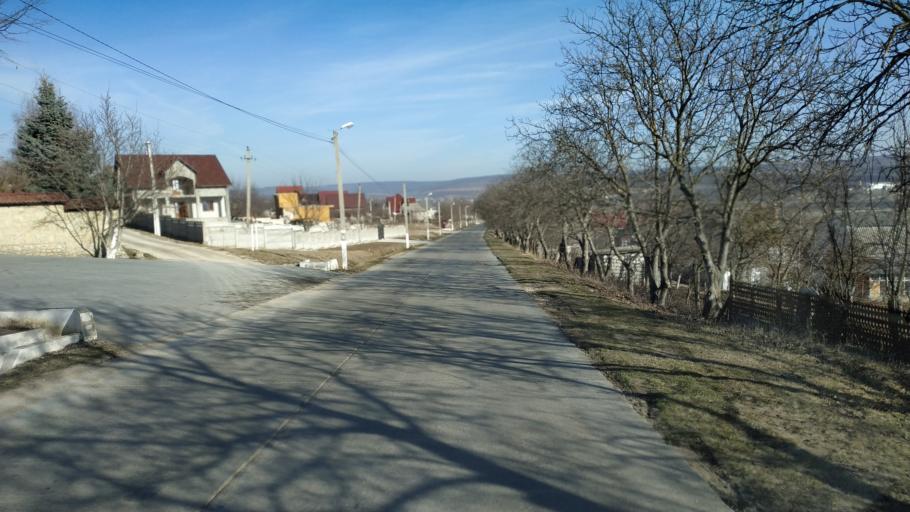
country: MD
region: Chisinau
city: Vatra
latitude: 46.9920
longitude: 28.6737
